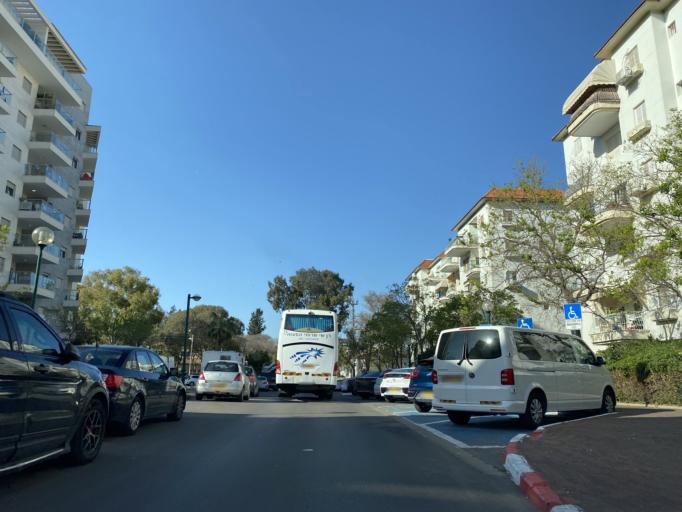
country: IL
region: Central District
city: Kfar Saba
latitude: 32.1800
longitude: 34.9158
